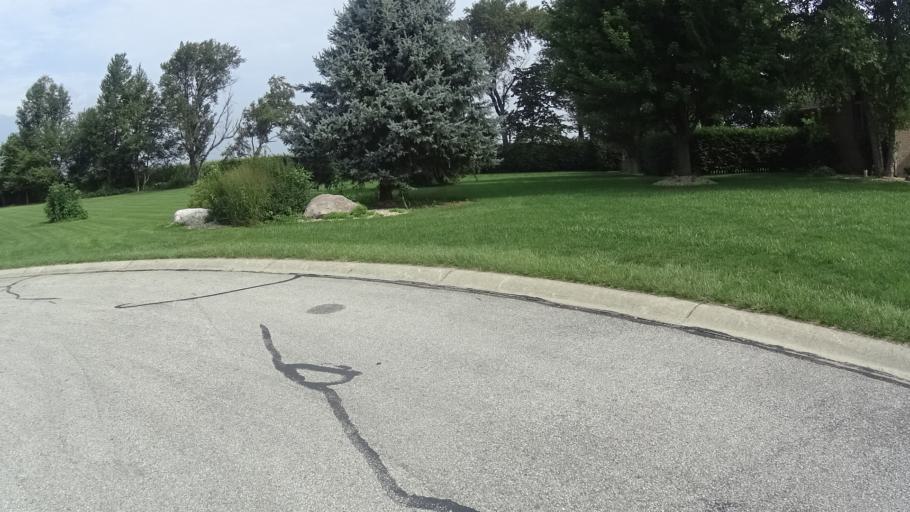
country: US
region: Indiana
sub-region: Madison County
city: Pendleton
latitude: 40.0131
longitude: -85.7946
